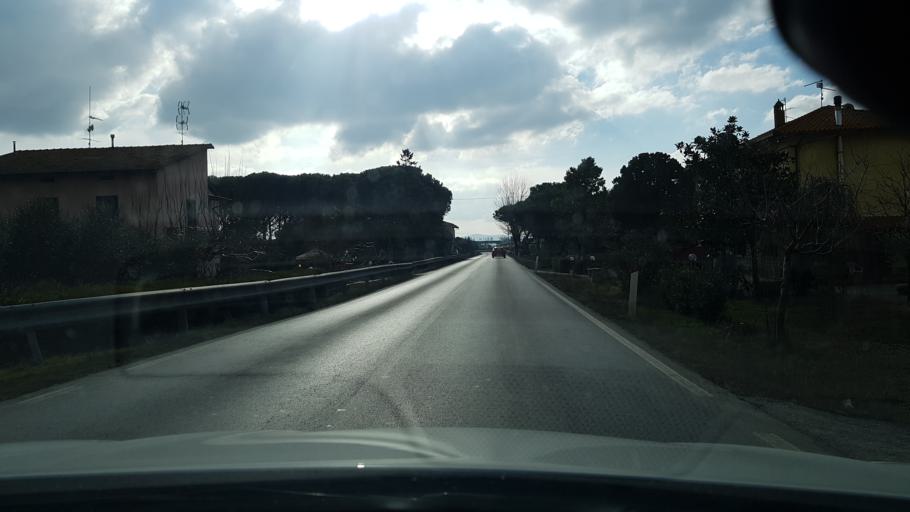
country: IT
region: Umbria
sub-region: Provincia di Perugia
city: Castiglione del Lago
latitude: 43.1528
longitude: 12.0201
